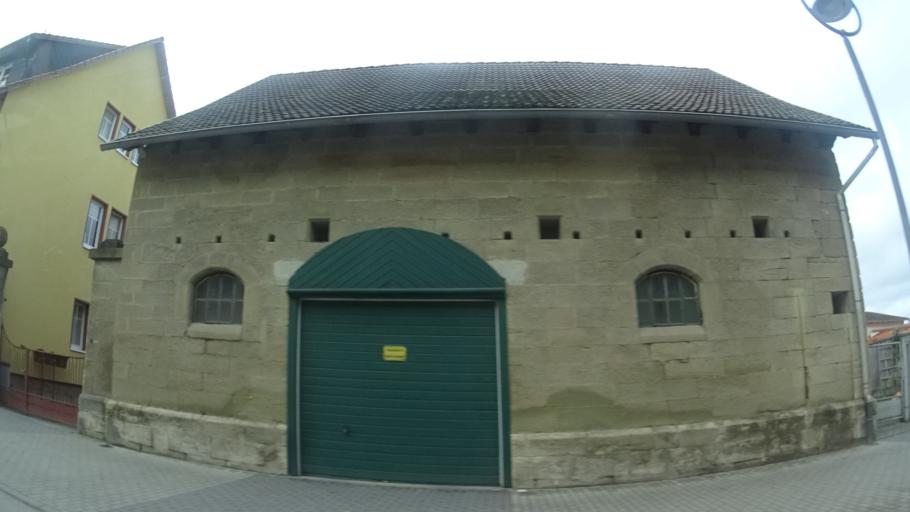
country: DE
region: Thuringia
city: Romhild
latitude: 50.3992
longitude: 10.5412
